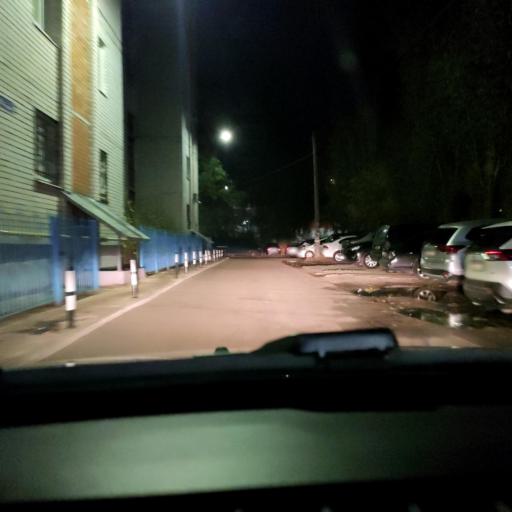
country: RU
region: Voronezj
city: Podgornoye
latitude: 51.7102
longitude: 39.1687
